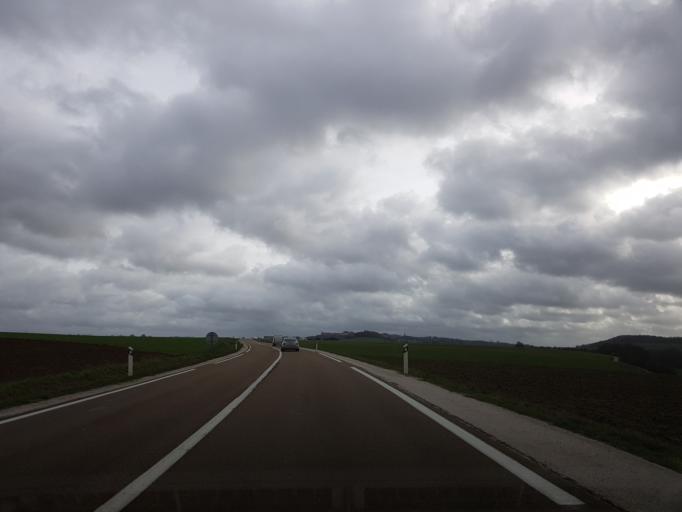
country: FR
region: Champagne-Ardenne
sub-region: Departement de la Haute-Marne
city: Langres
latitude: 47.8988
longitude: 5.3081
